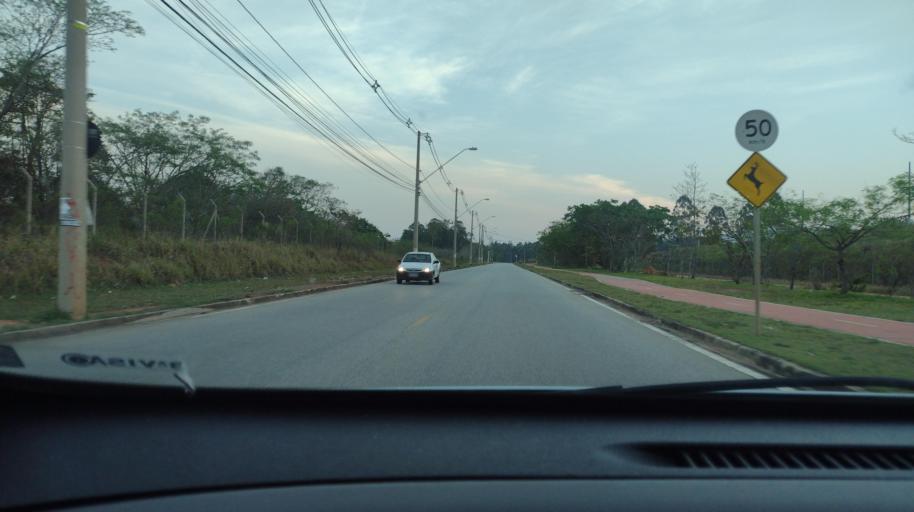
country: BR
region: Sao Paulo
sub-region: Sorocaba
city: Sorocaba
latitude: -23.3715
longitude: -47.4733
